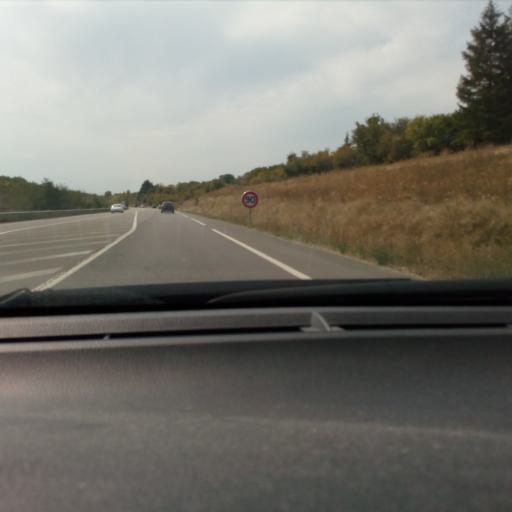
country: FR
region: Poitou-Charentes
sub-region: Departement de la Charente
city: Saint-Saturnin
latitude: 45.6756
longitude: 0.0478
